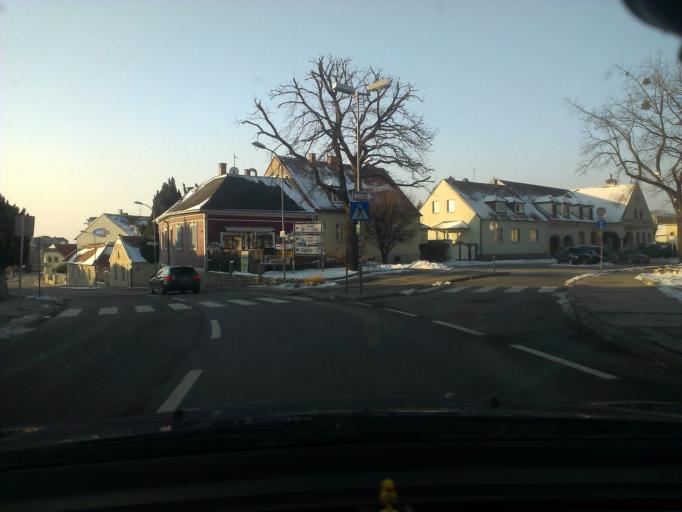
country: AT
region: Burgenland
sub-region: Eisenstadt Stadt
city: Eisenstadt
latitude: 47.8449
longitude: 16.5262
